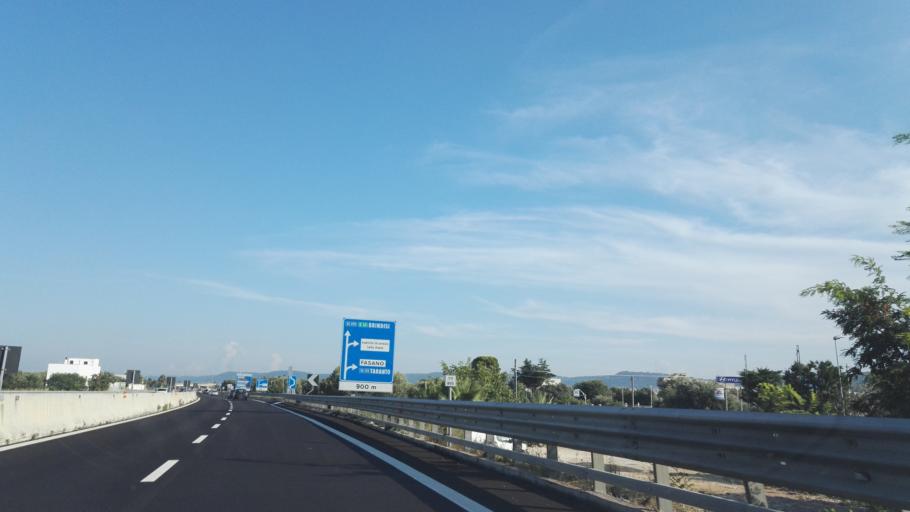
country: IT
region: Apulia
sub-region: Provincia di Brindisi
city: Fasano
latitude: 40.8578
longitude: 17.3503
